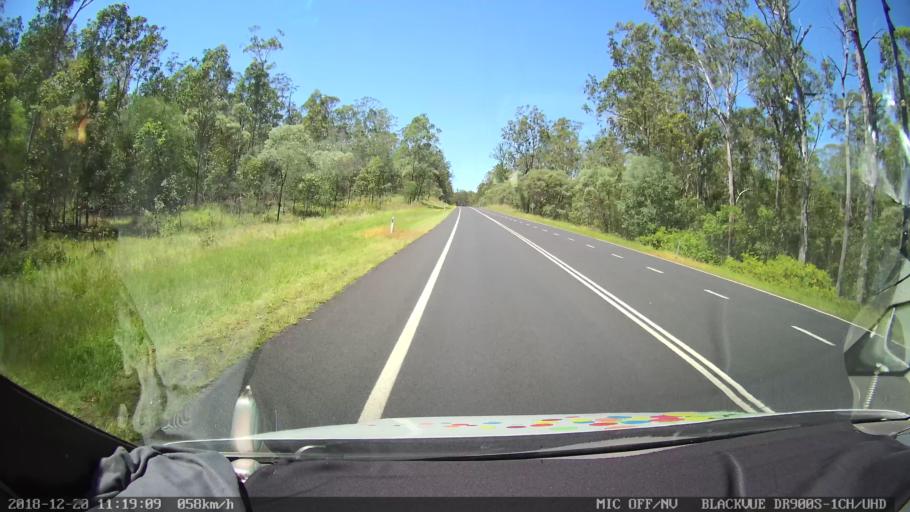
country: AU
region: New South Wales
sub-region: Richmond Valley
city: Casino
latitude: -29.0591
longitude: 153.0051
